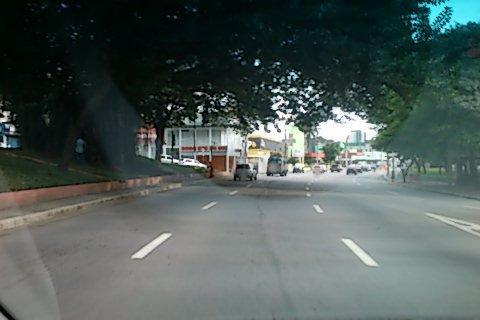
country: BR
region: Sao Paulo
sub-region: Sao Jose Dos Campos
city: Sao Jose dos Campos
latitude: -23.2034
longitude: -45.8846
